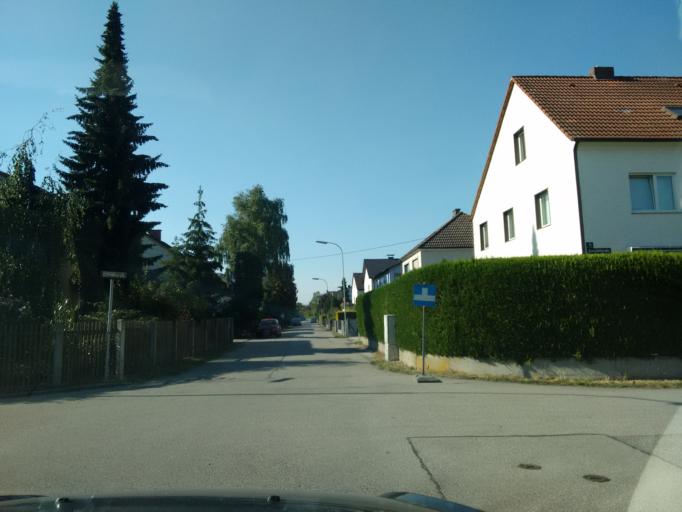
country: AT
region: Upper Austria
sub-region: Politischer Bezirk Linz-Land
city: Traun
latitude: 48.2285
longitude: 14.2471
